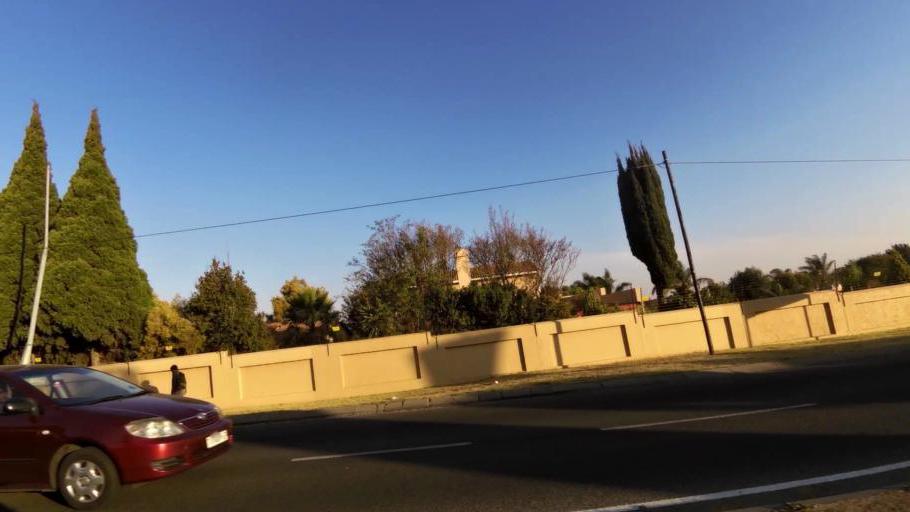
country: ZA
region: Gauteng
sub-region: City of Johannesburg Metropolitan Municipality
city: Roodepoort
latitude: -26.1639
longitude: 27.9526
